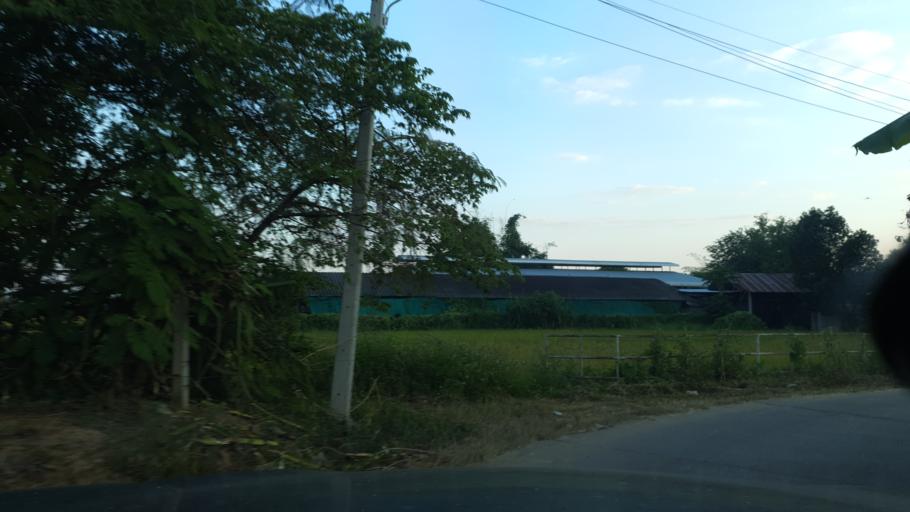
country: TH
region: Chiang Mai
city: San Sai
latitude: 18.8693
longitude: 99.0775
